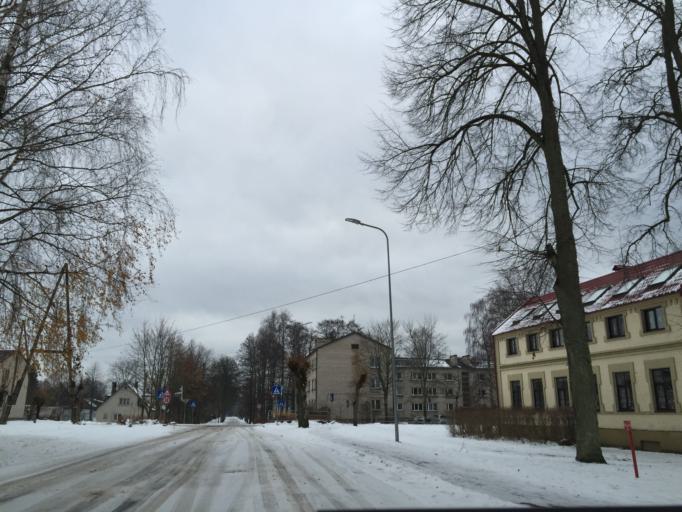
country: LV
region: Saulkrastu
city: Saulkrasti
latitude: 57.2641
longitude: 24.4180
